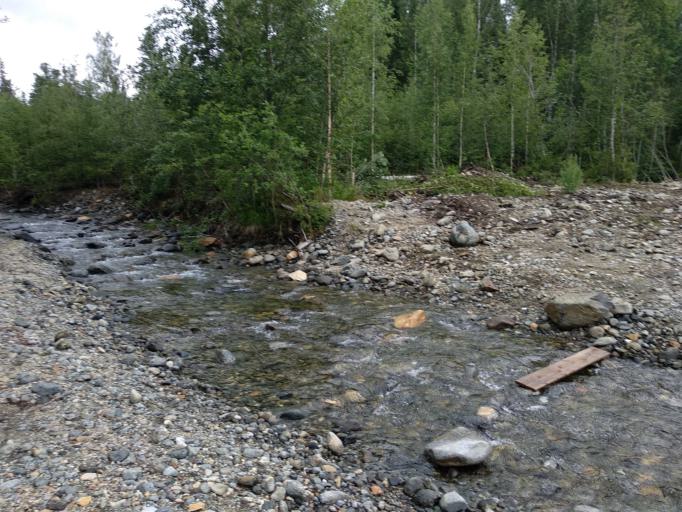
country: RU
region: Sverdlovsk
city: Karpinsk
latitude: 59.5928
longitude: 59.4074
